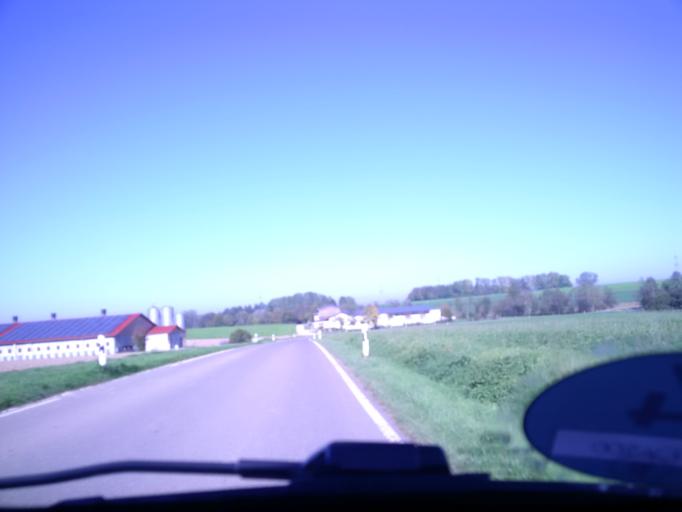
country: DE
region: Baden-Wuerttemberg
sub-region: Tuebingen Region
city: Huttisheim
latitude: 48.2886
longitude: 9.9345
